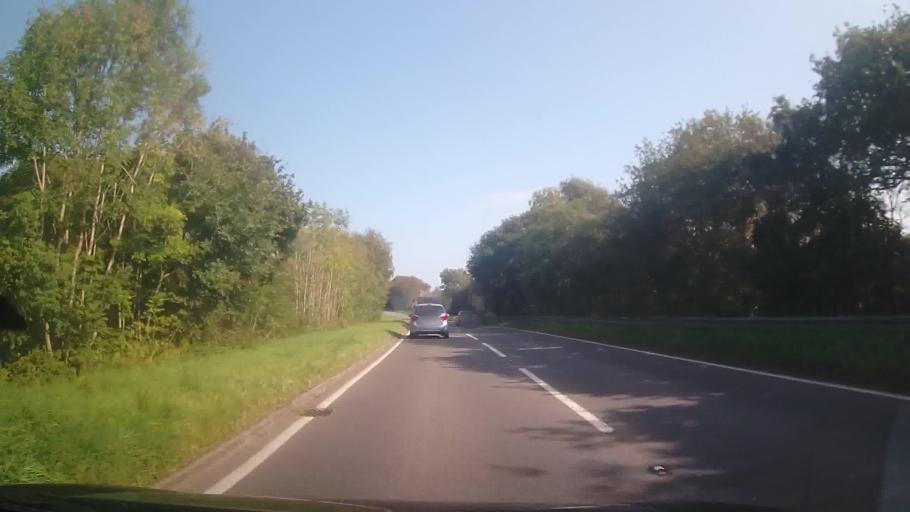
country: GB
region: Wales
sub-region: Pembrokeshire
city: Nevern
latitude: 52.0163
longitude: -4.8071
